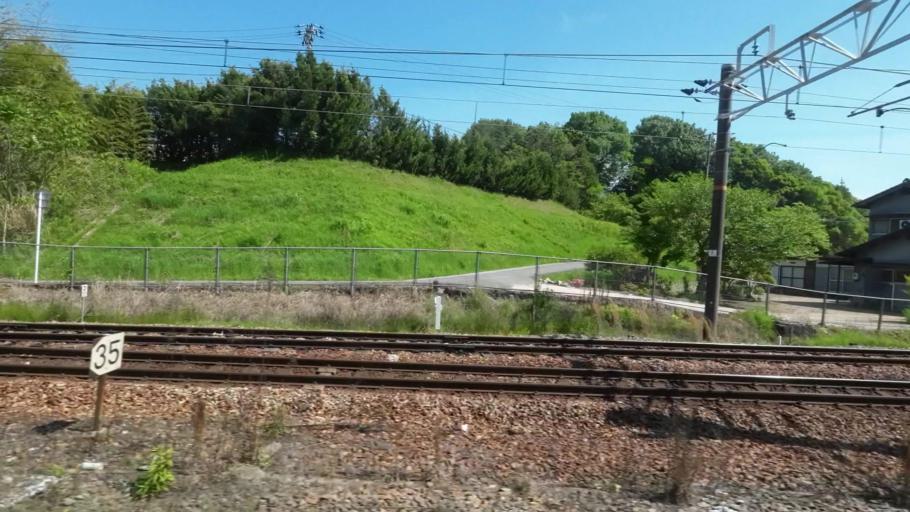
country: JP
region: Hiroshima
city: Fukuyama
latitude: 34.4734
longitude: 133.3081
